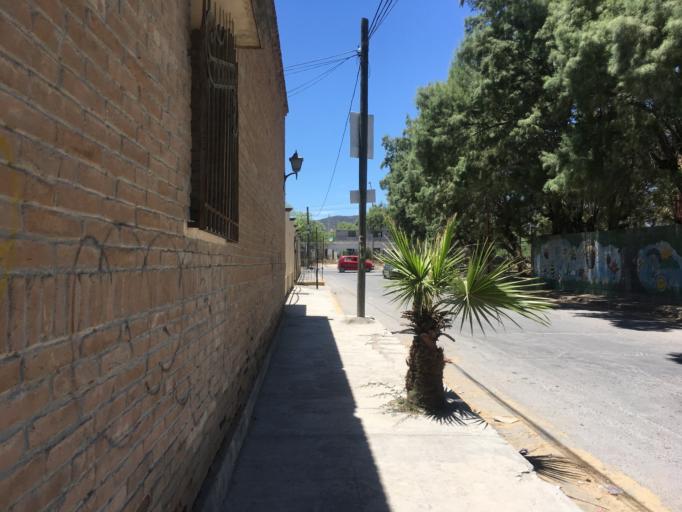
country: MX
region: Nuevo Leon
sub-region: Garcia
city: Las Torres de Guadalupe
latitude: 25.8099
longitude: -100.6121
